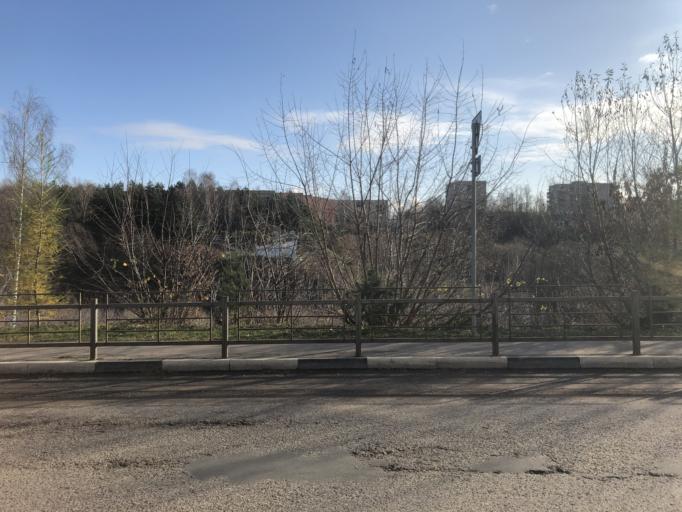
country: RU
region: Tverskaya
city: Rzhev
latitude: 56.2612
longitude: 34.3395
